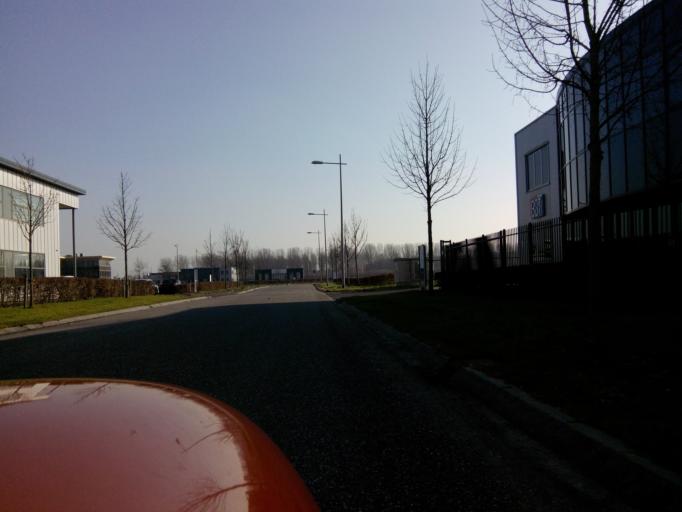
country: NL
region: Flevoland
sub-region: Gemeente Zeewolde
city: Zeewolde
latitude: 52.3504
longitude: 5.4948
